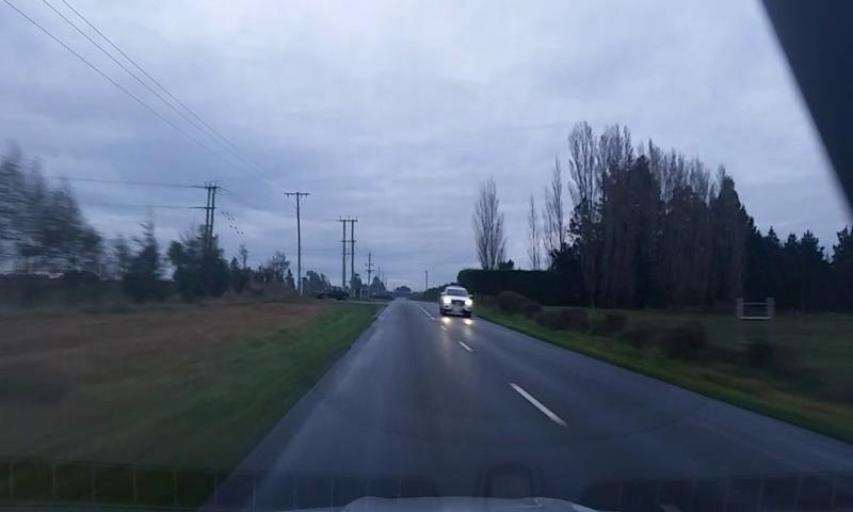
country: NZ
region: Canterbury
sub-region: Ashburton District
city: Rakaia
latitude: -43.7585
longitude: 171.9608
